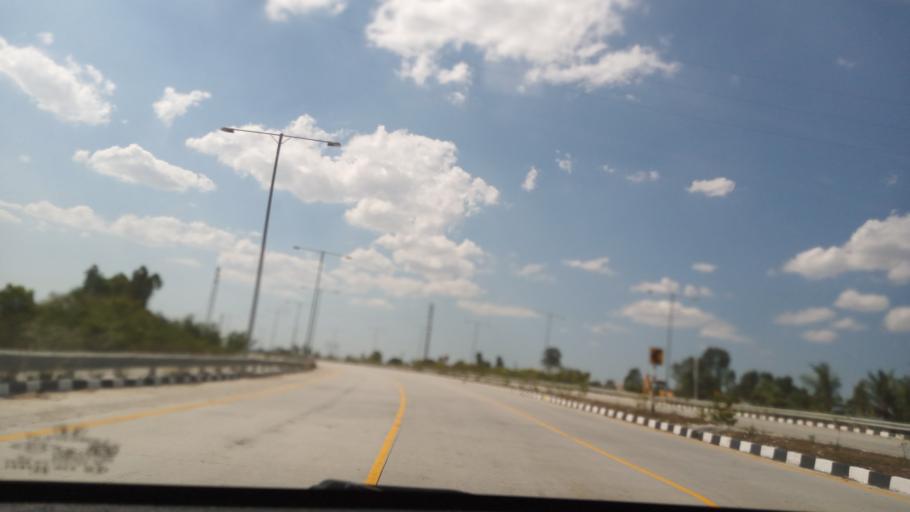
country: IN
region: Andhra Pradesh
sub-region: Chittoor
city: Palmaner
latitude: 13.2210
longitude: 78.7417
